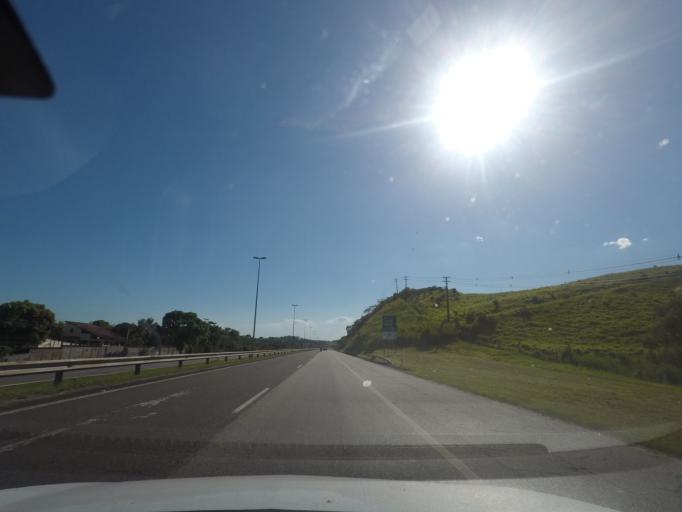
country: BR
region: Rio de Janeiro
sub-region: Guapimirim
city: Guapimirim
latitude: -22.6469
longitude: -43.0714
